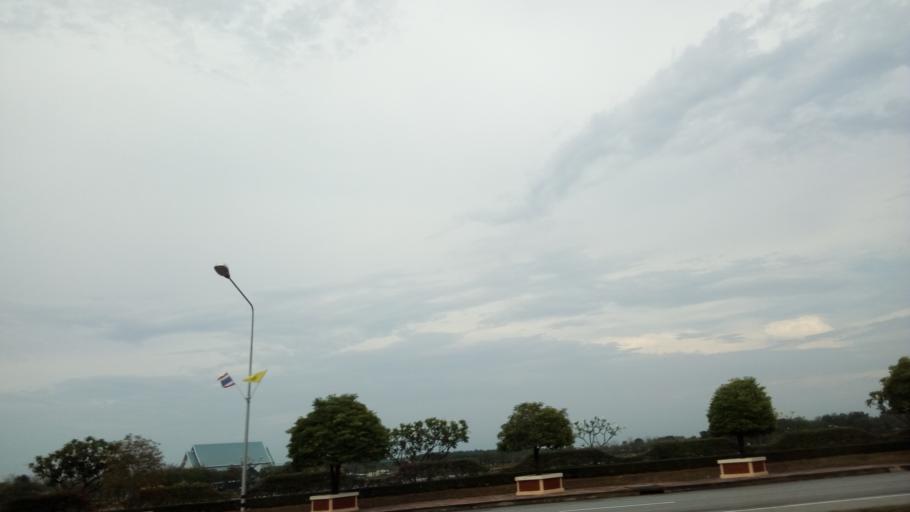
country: TH
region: Phra Nakhon Si Ayutthaya
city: Bang Pa-in
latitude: 14.2084
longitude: 100.5468
